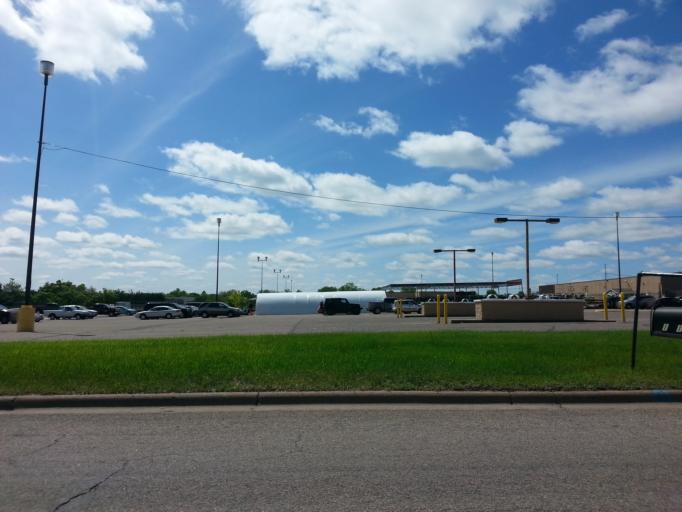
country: US
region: Wisconsin
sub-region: Saint Croix County
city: Hudson
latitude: 44.9581
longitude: -92.7342
